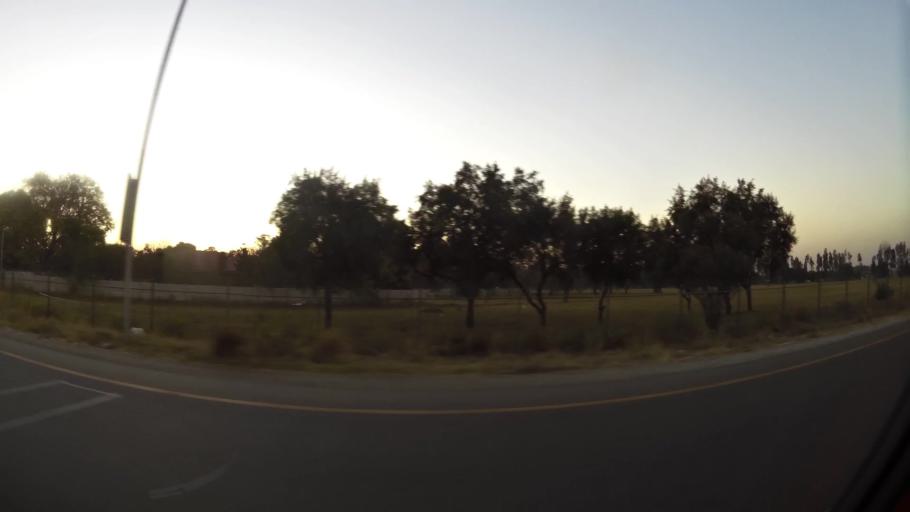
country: ZA
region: North-West
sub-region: Bojanala Platinum District Municipality
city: Rustenburg
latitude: -25.6440
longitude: 27.2599
